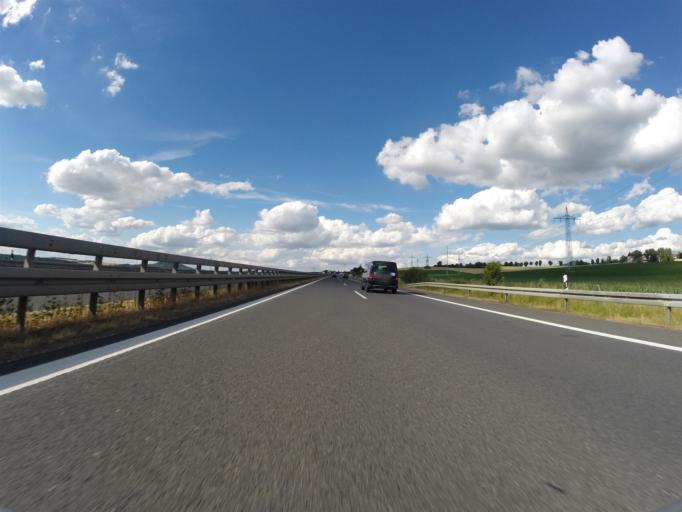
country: DE
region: Bavaria
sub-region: Upper Franconia
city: Ebensfeld
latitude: 50.0497
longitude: 10.9603
